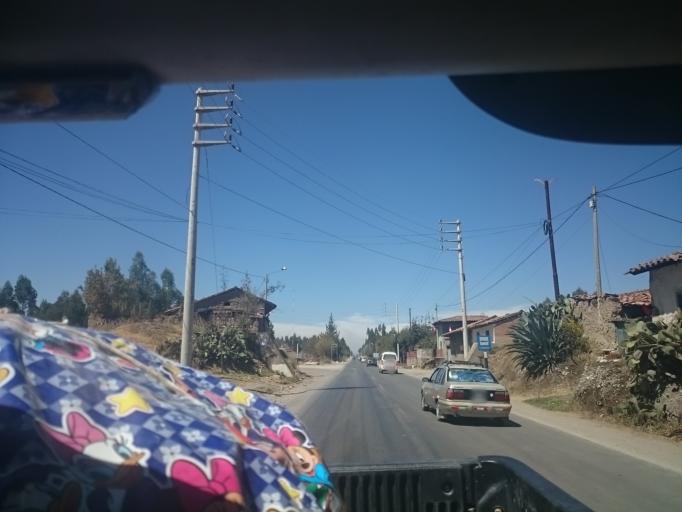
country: PE
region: Junin
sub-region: Provincia de Concepcion
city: Matahuasi
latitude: -11.8973
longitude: -75.3389
